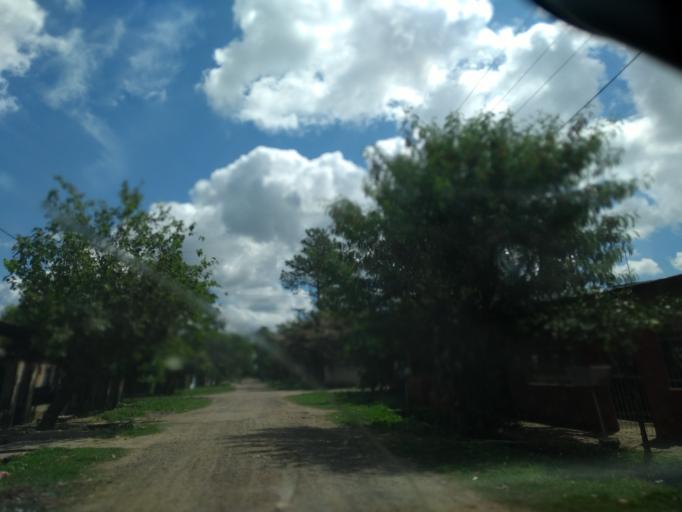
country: AR
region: Chaco
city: Fontana
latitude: -27.4191
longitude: -59.0504
